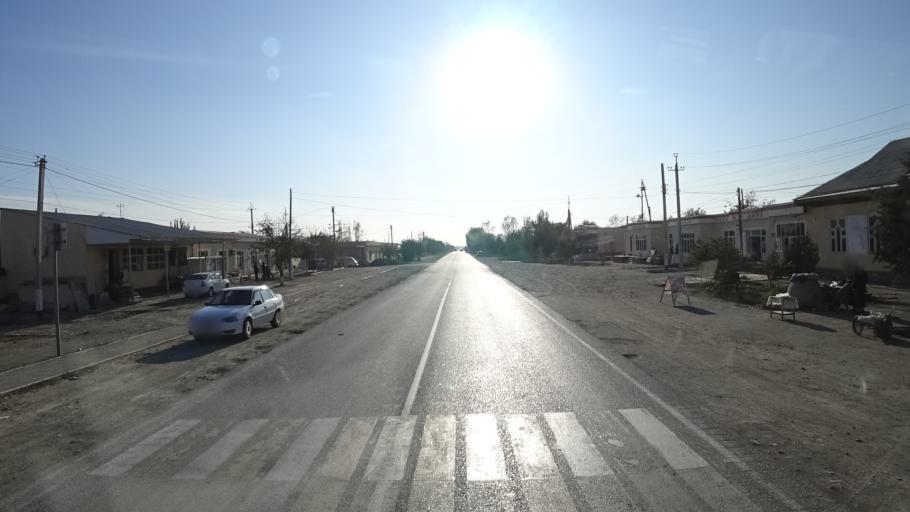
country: UZ
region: Navoiy
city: Beshrabot
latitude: 40.1862
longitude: 65.3580
